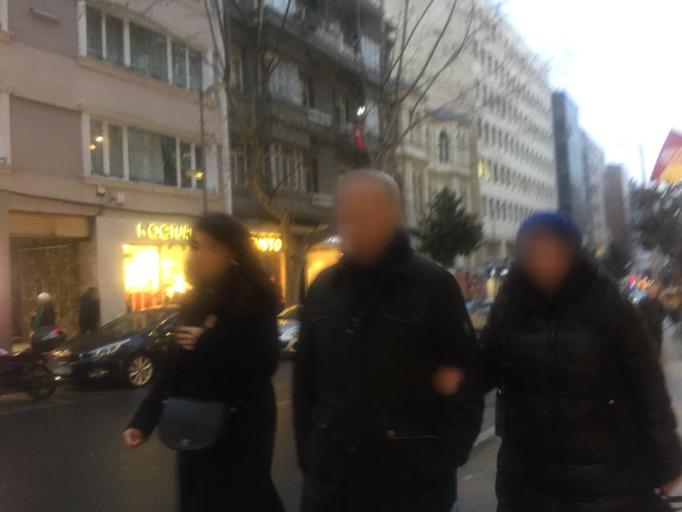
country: TR
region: Istanbul
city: Sisli
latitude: 41.0525
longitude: 28.9905
